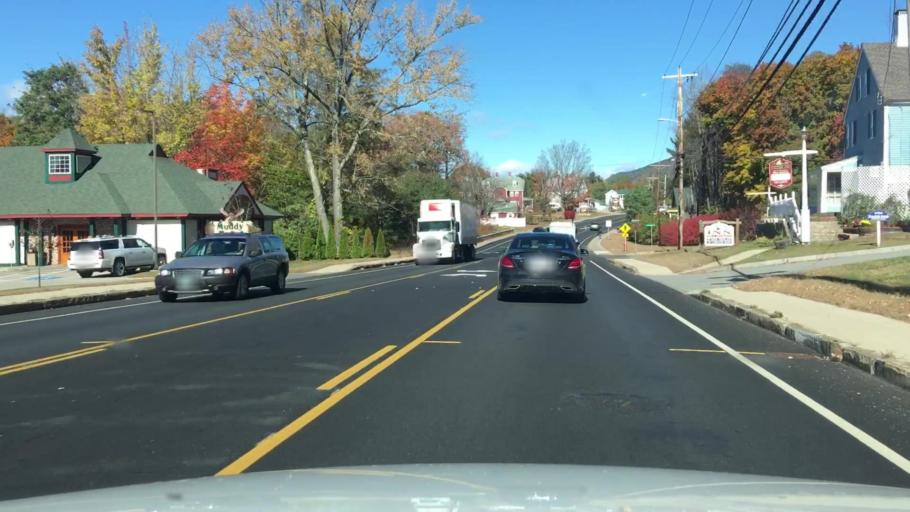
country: US
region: New Hampshire
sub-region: Carroll County
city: North Conway
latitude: 44.0435
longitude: -71.1246
